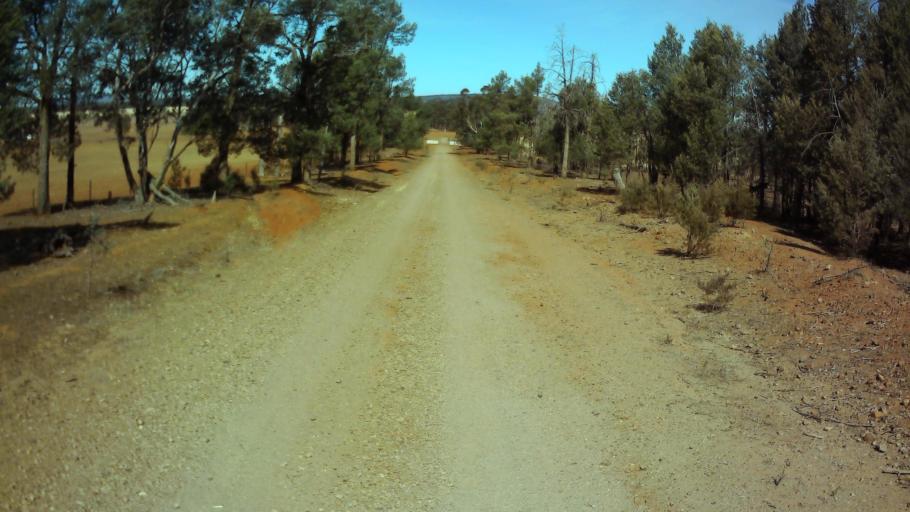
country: AU
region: New South Wales
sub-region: Weddin
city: Grenfell
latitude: -33.7822
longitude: 147.7606
